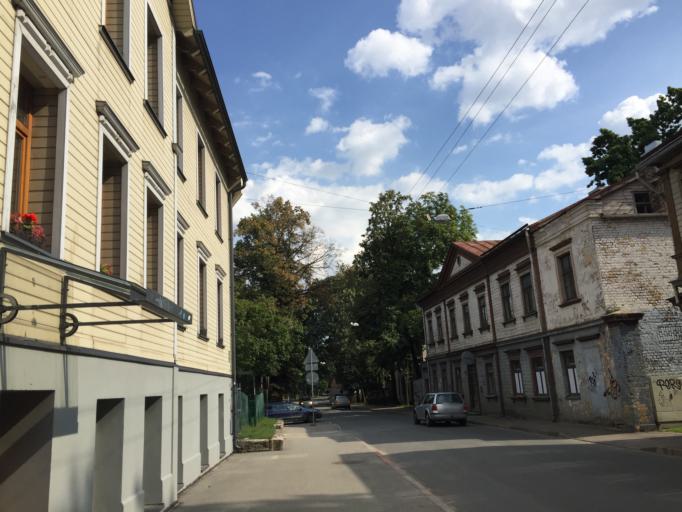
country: LV
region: Riga
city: Riga
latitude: 56.9344
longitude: 24.0746
